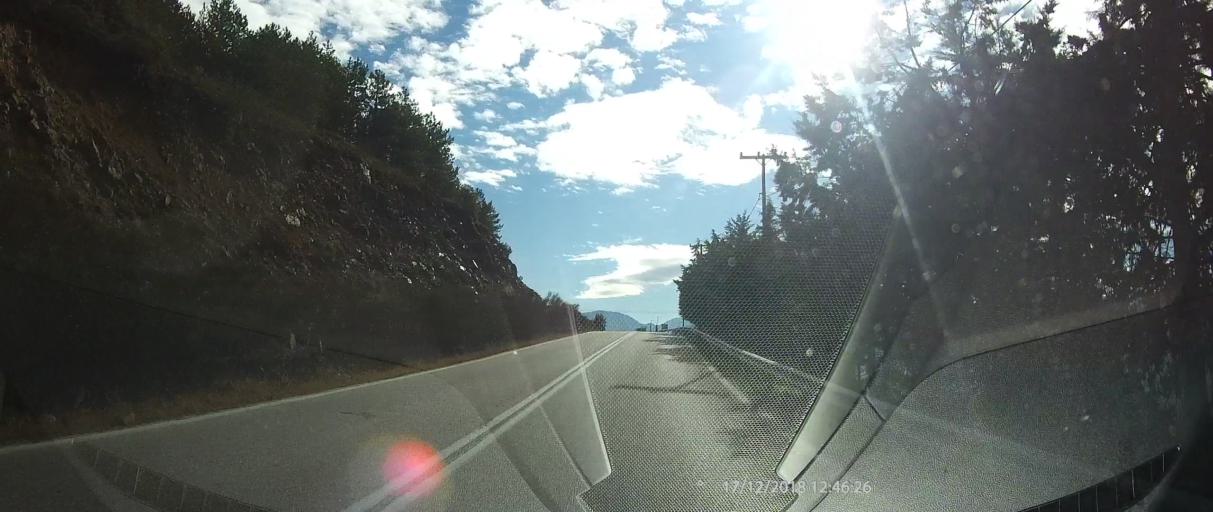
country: GR
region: Thessaly
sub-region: Trikala
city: Kastraki
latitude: 39.7867
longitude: 21.4175
